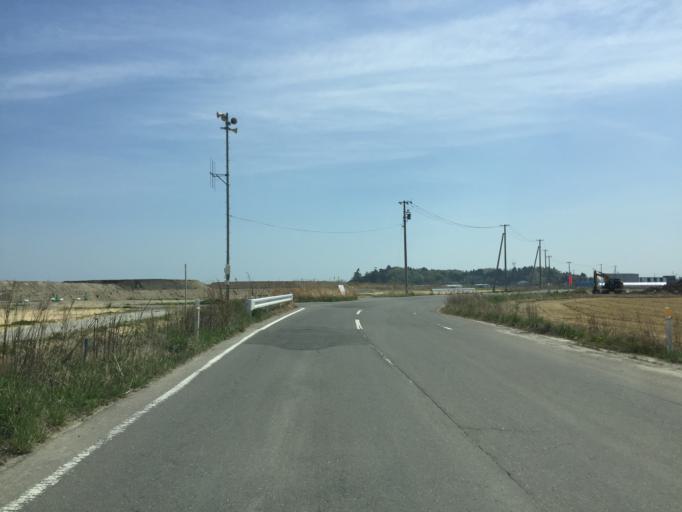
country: JP
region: Miyagi
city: Watari
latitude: 37.9069
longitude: 140.9223
